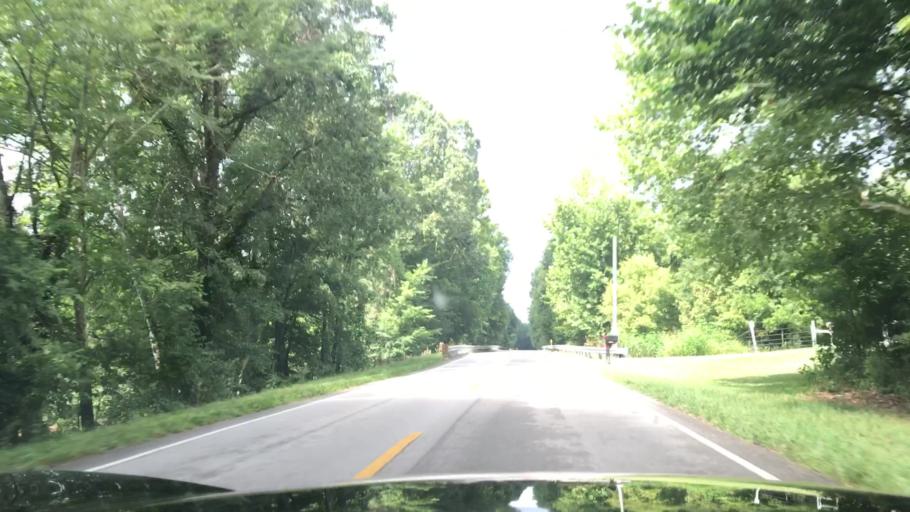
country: US
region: Kentucky
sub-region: Butler County
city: Morgantown
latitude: 37.1844
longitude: -86.7717
